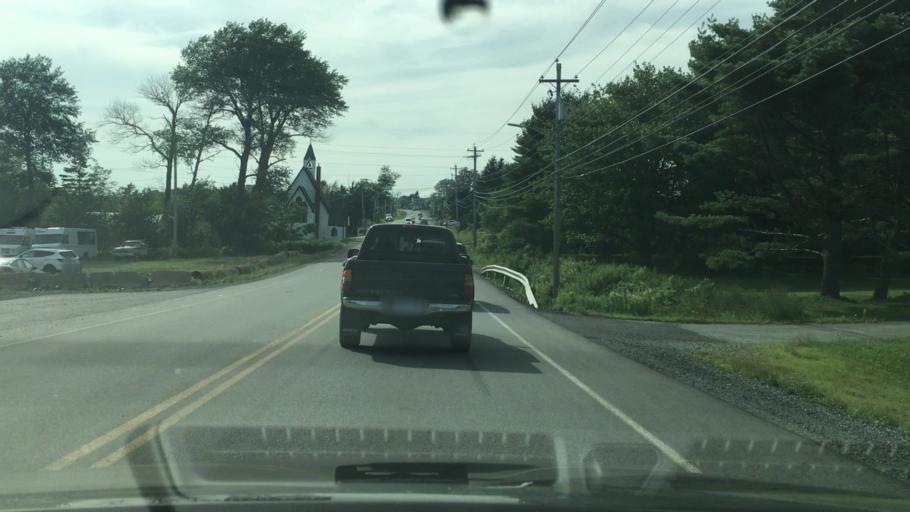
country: CA
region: Nova Scotia
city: Dartmouth
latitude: 44.7315
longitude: -63.7567
